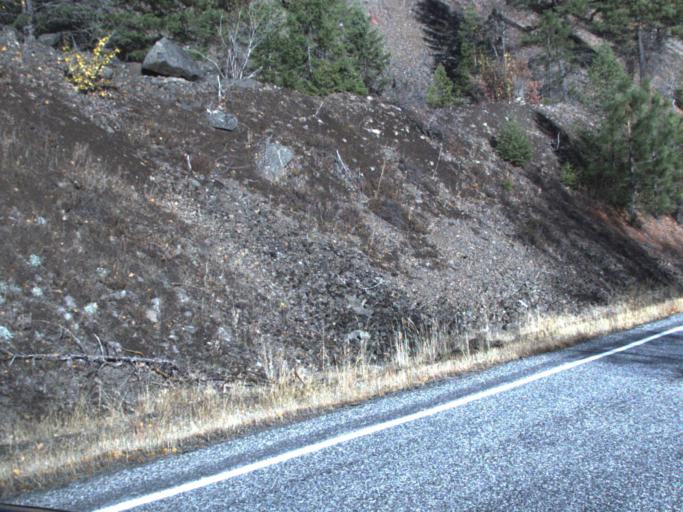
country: US
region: Washington
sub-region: Ferry County
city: Republic
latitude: 48.3483
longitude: -118.7462
